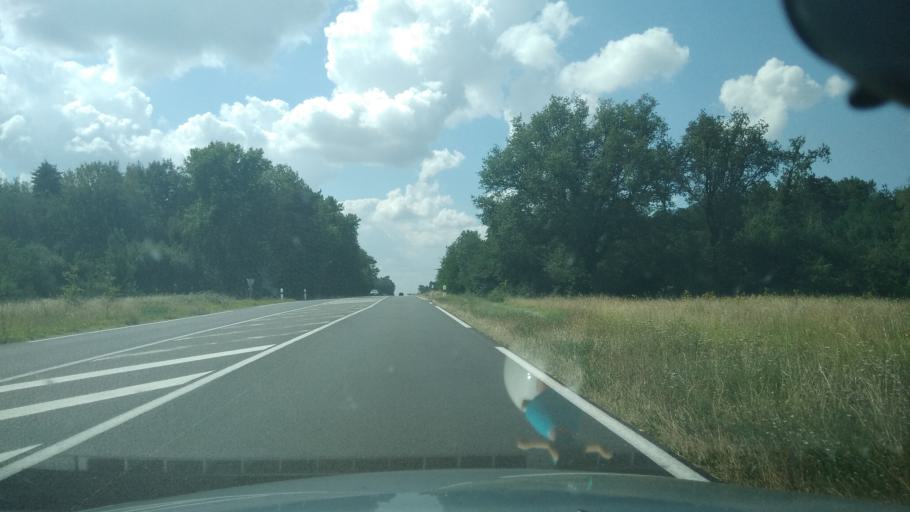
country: FR
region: Centre
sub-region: Departement d'Indre-et-Loire
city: Sainte-Maure-de-Touraine
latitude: 47.0709
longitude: 0.6140
